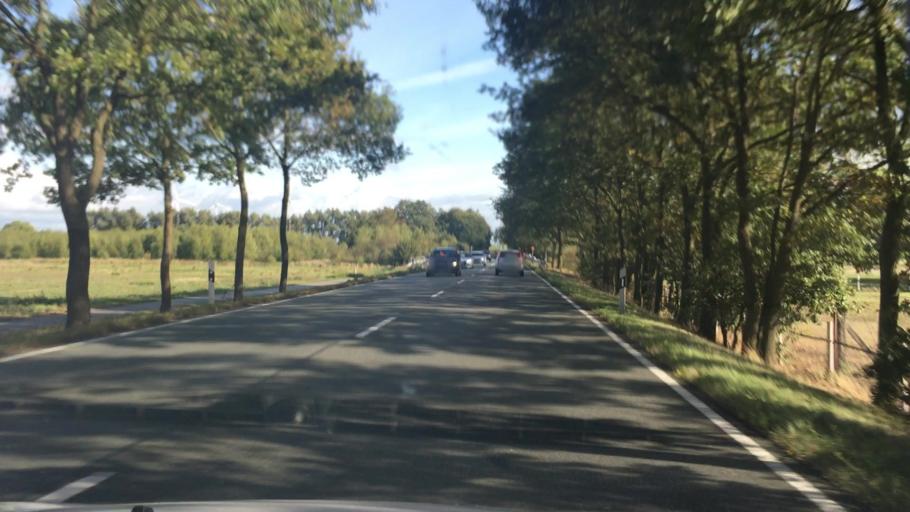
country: DE
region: Lower Saxony
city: Siedenburg
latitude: 52.6752
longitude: 8.9164
